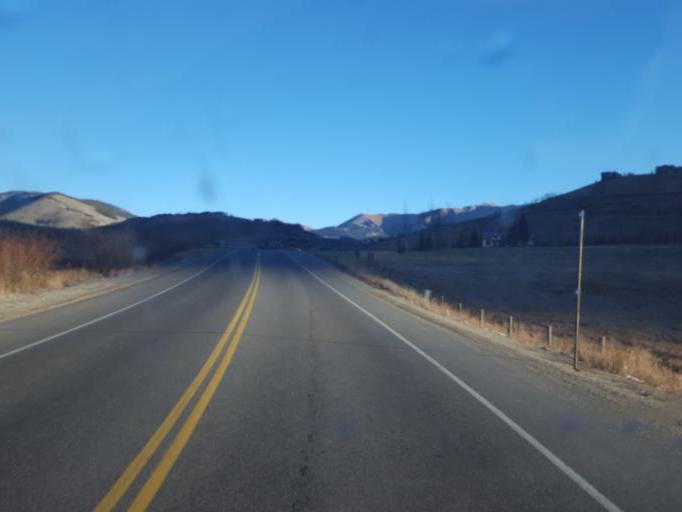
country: US
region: Colorado
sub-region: Gunnison County
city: Crested Butte
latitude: 38.8837
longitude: -106.9714
